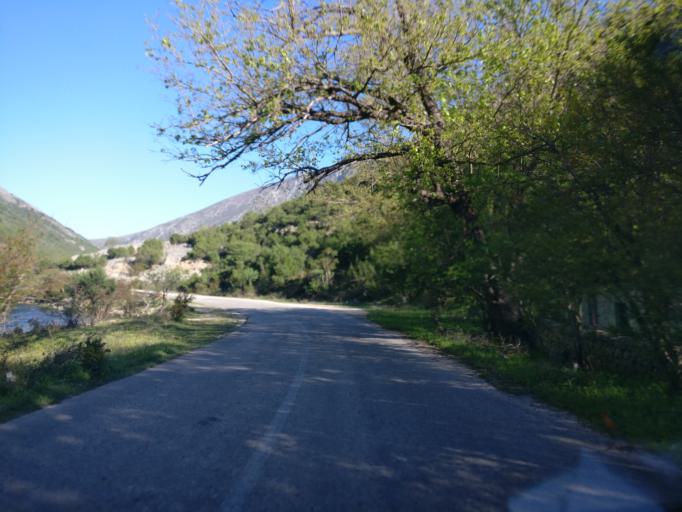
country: BA
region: Federation of Bosnia and Herzegovina
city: Stolac
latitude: 43.0824
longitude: 18.0105
